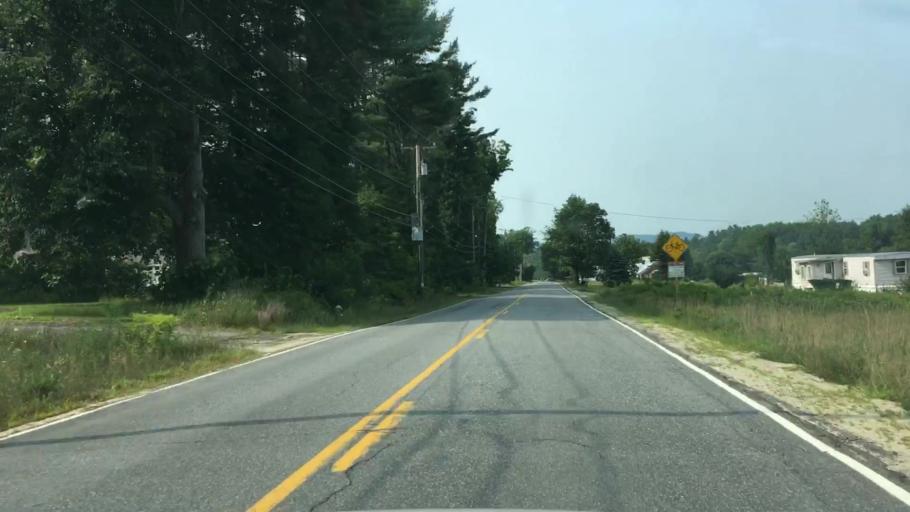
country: US
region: Maine
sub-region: Oxford County
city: Norway
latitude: 44.2237
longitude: -70.5927
